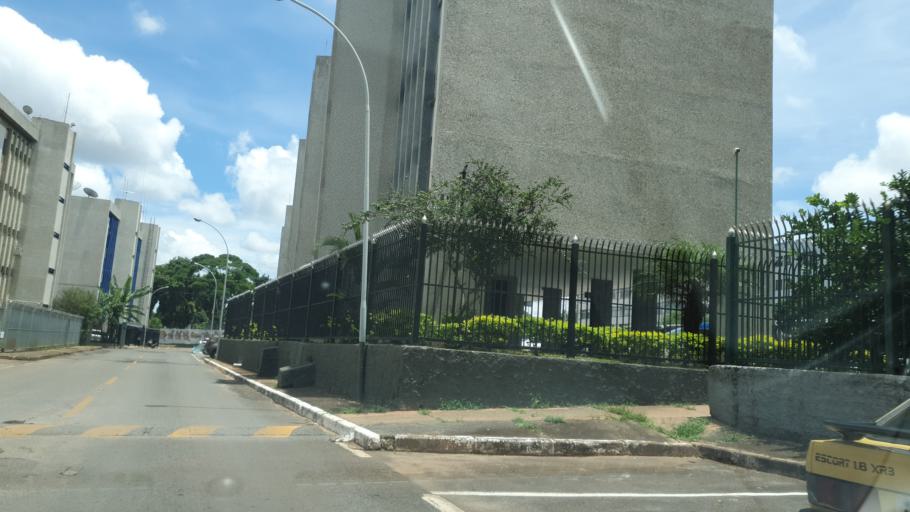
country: BR
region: Federal District
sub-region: Brasilia
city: Brasilia
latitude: -15.7950
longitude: -47.9421
